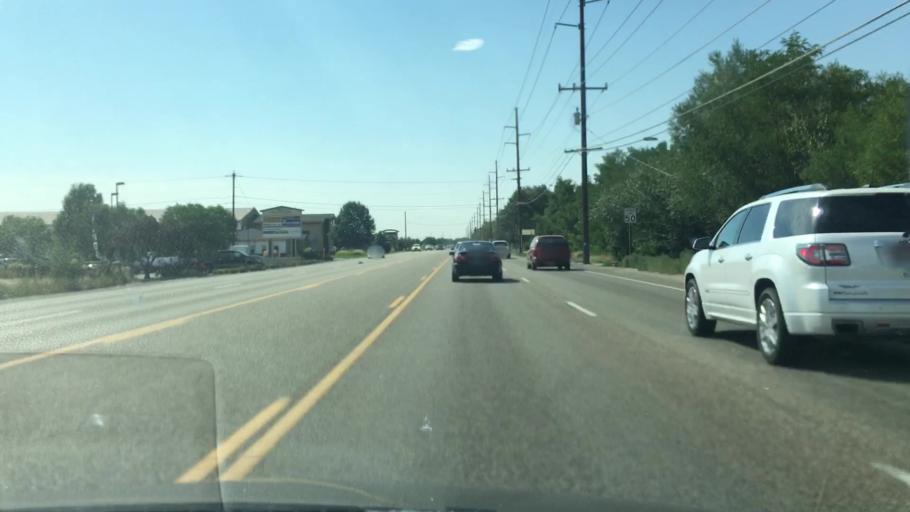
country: US
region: Idaho
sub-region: Ada County
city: Eagle
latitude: 43.6786
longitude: -116.3024
